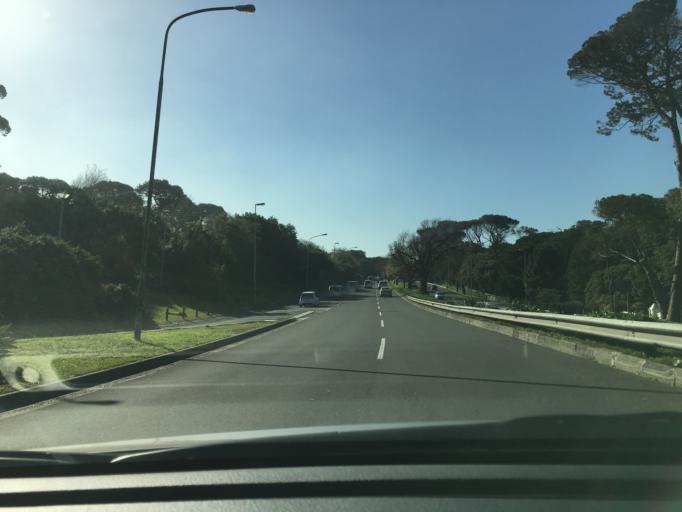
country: ZA
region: Western Cape
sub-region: City of Cape Town
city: Claremont
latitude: -33.9645
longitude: 18.4592
